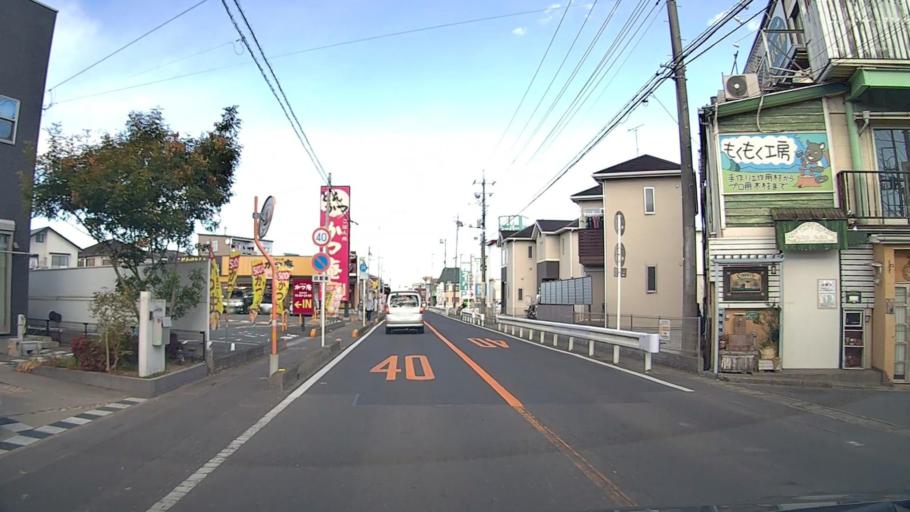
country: JP
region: Saitama
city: Asaka
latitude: 35.7808
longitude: 139.5723
